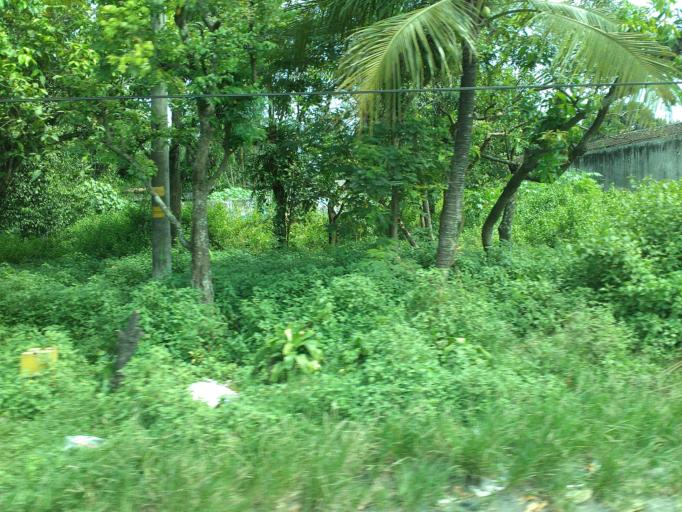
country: ID
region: Central Java
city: Candi Prambanan
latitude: -7.7545
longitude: 110.5098
